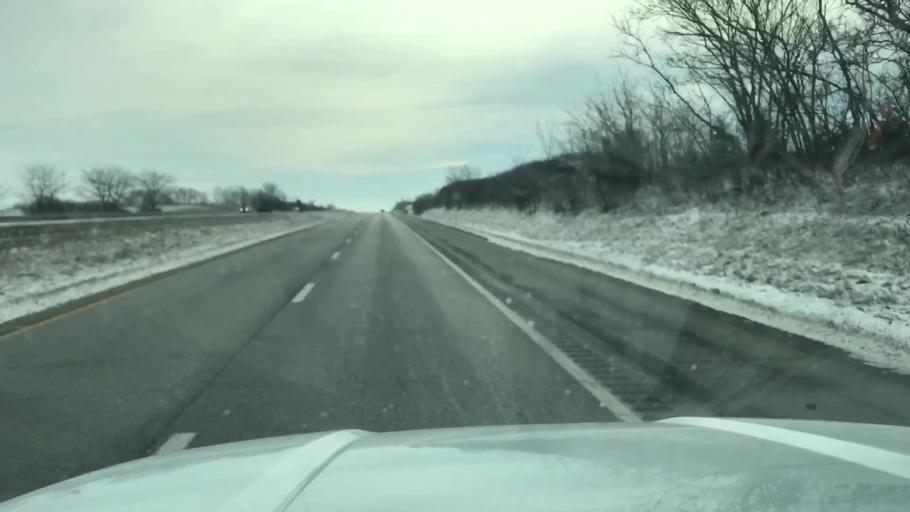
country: US
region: Missouri
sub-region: Andrew County
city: Savannah
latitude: 39.9526
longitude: -94.9528
